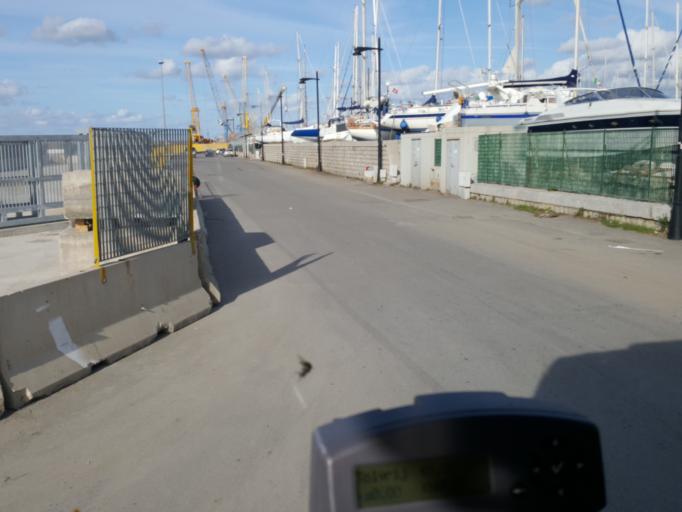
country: IT
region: Sicily
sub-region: Palermo
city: Termini Imerese
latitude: 37.9843
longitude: 13.7040
